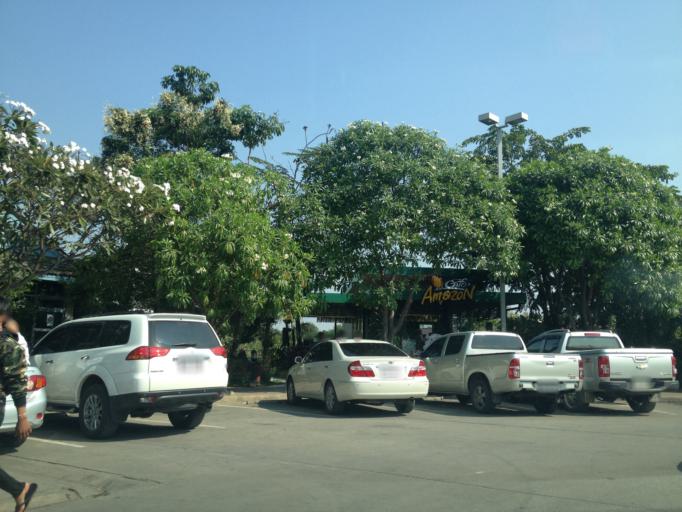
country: TH
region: Chiang Mai
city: Hot
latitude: 18.1935
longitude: 98.6069
